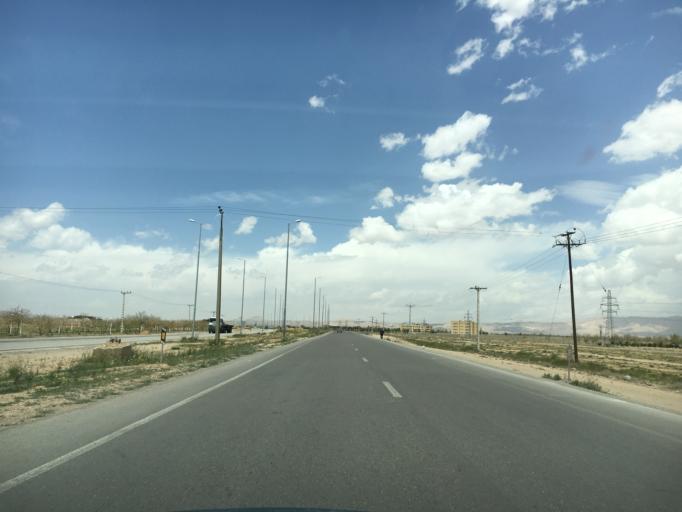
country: IR
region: Isfahan
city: Kashan
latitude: 33.4570
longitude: 51.1693
